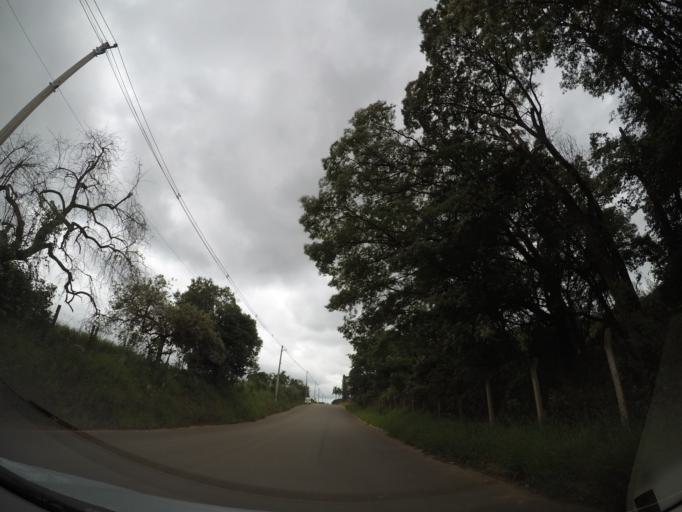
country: BR
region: Sao Paulo
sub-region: Itupeva
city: Itupeva
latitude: -23.1255
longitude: -47.0171
